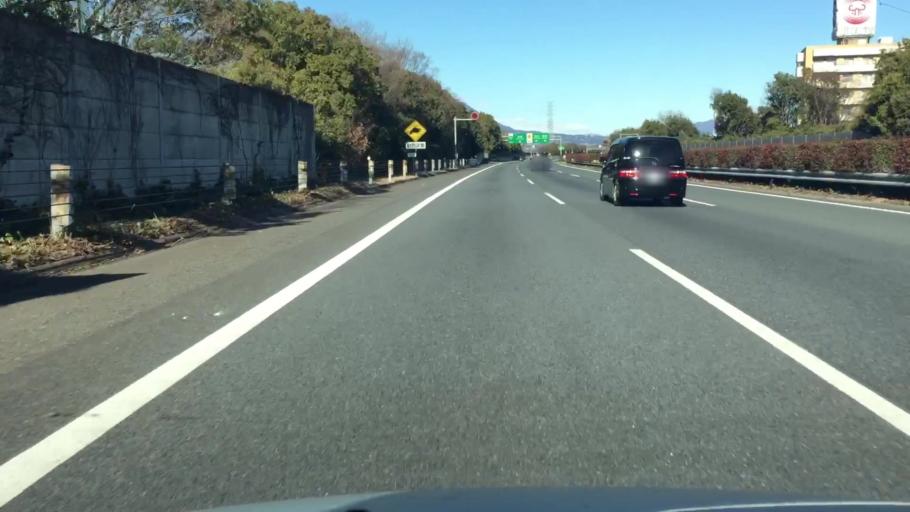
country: JP
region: Gunma
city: Takasaki
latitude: 36.3621
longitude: 139.0340
